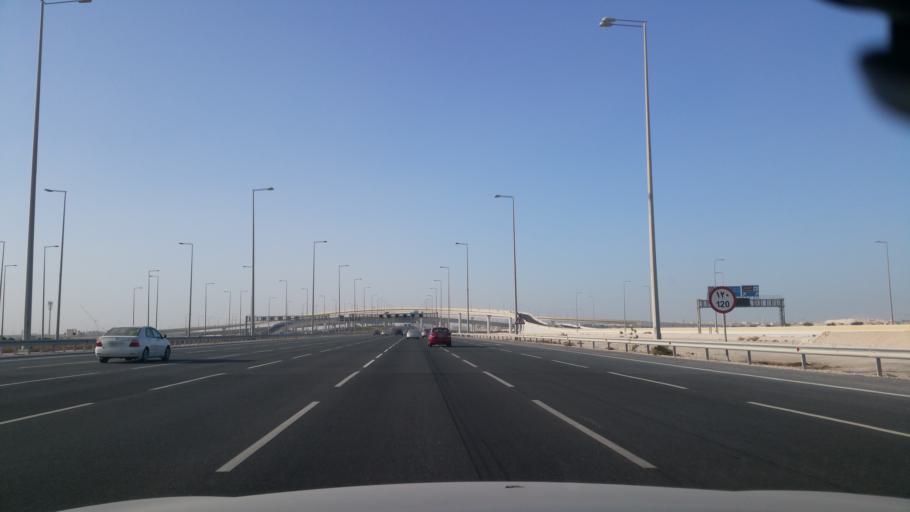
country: QA
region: Al Wakrah
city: Al Wukayr
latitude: 25.1949
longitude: 51.5444
